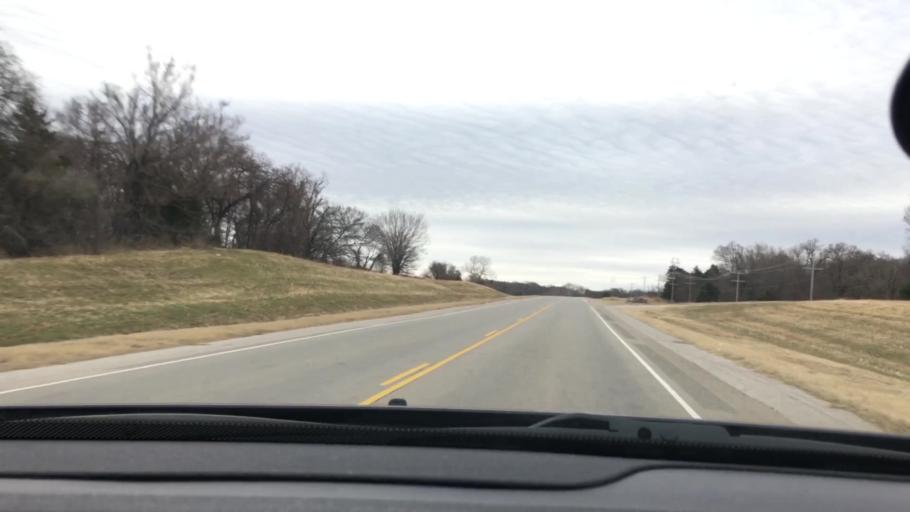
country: US
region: Oklahoma
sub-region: Johnston County
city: Tishomingo
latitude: 34.2332
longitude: -96.7889
